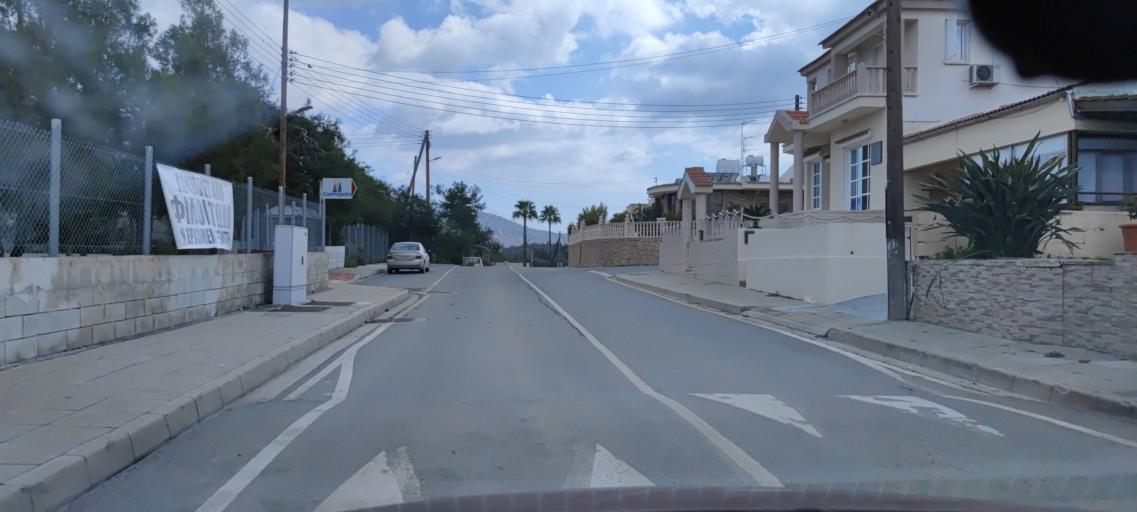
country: CY
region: Larnaka
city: Kornos
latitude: 34.9154
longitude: 33.4019
